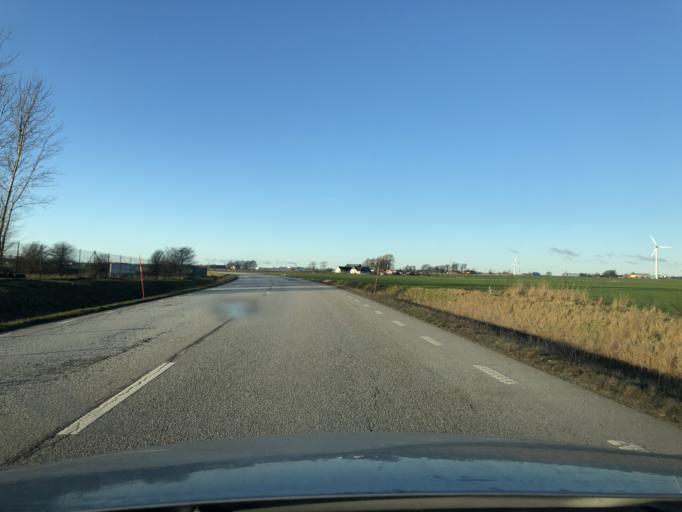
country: SE
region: Skane
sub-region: Trelleborgs Kommun
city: Trelleborg
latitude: 55.3548
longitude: 13.2550
